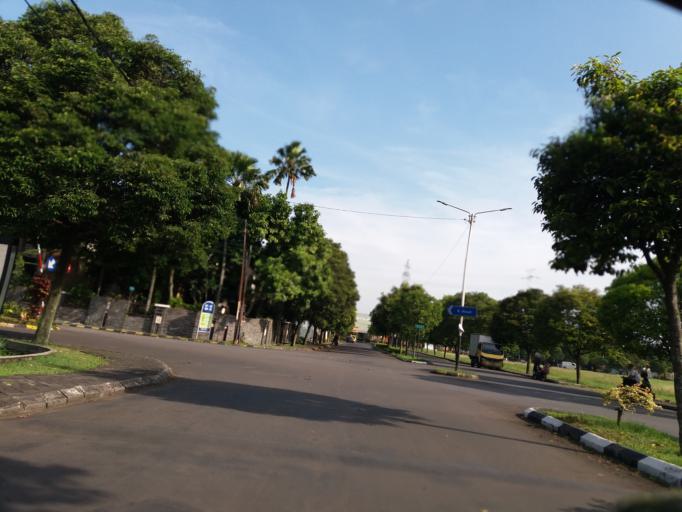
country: ID
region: West Java
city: Bandung
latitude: -6.9615
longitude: 107.6273
